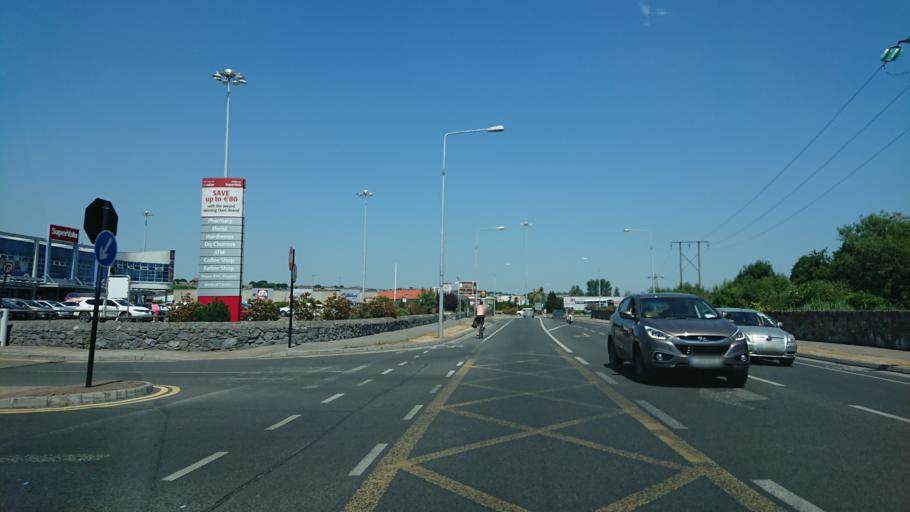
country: IE
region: Munster
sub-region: Waterford
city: Waterford
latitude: 52.2457
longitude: -7.1202
